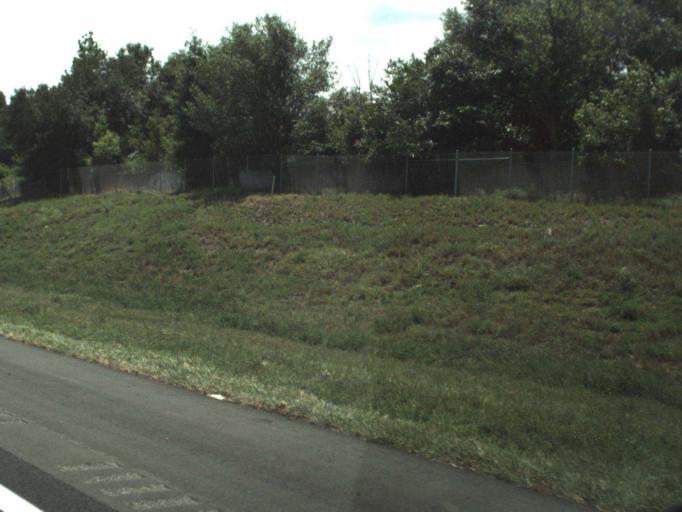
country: US
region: Florida
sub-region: Seminole County
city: Heathrow
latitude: 28.7289
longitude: -81.3732
